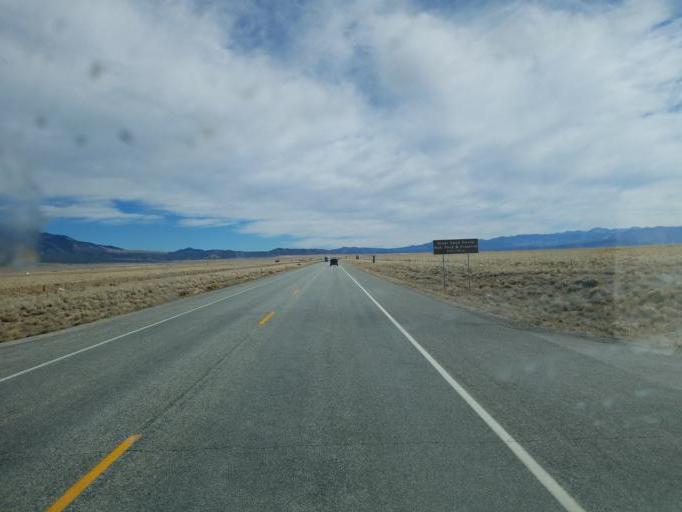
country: US
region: Colorado
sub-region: Alamosa County
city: Alamosa East
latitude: 37.4750
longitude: -105.6212
